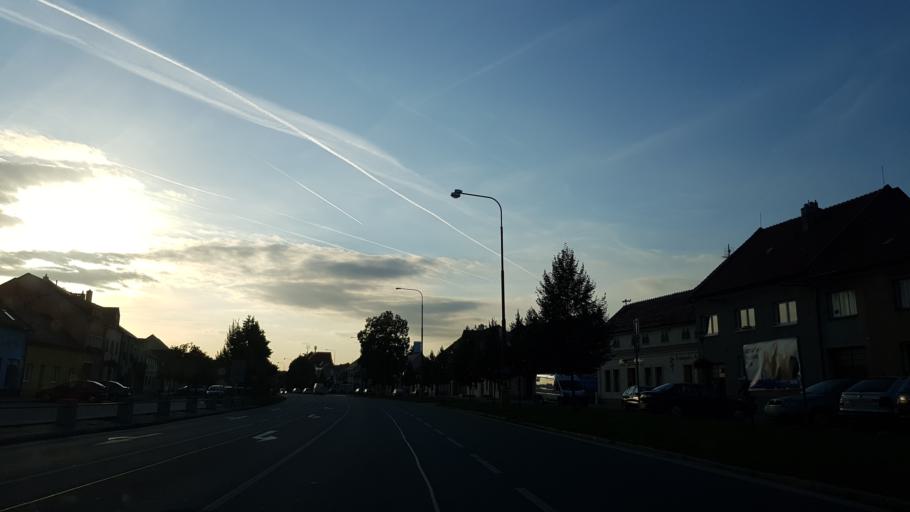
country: CZ
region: Zlin
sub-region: Okres Uherske Hradiste
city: Stare Mesto
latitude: 49.0760
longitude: 17.4471
